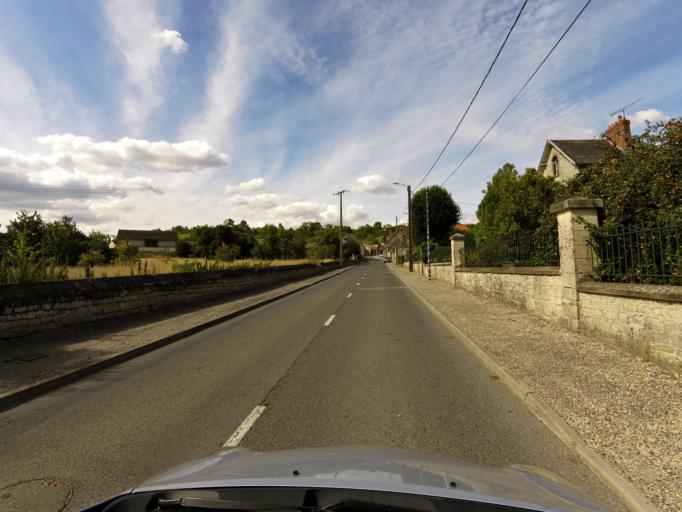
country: FR
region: Picardie
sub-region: Departement de l'Aisne
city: Bruyeres-et-Montberault
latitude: 49.4723
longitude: 3.6648
